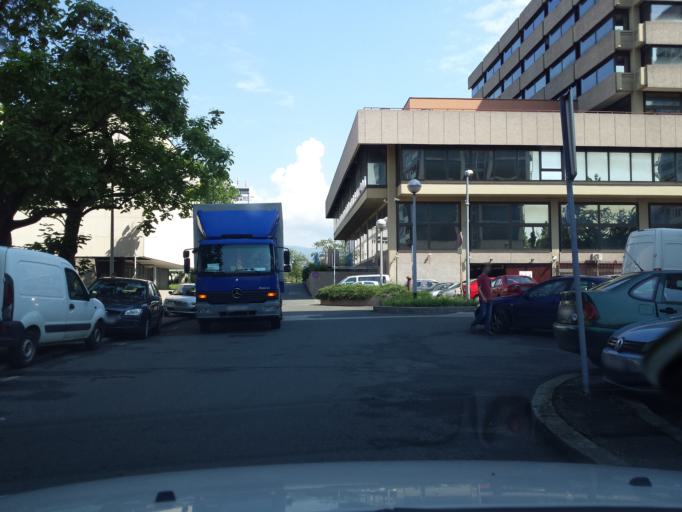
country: HR
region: Grad Zagreb
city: Zagreb - Centar
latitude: 45.7987
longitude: 15.9721
